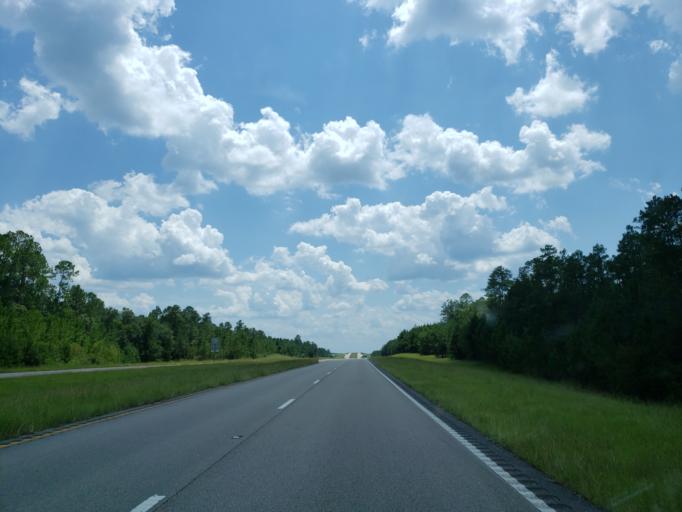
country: US
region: Mississippi
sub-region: Greene County
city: Leakesville
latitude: 31.1436
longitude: -88.5029
